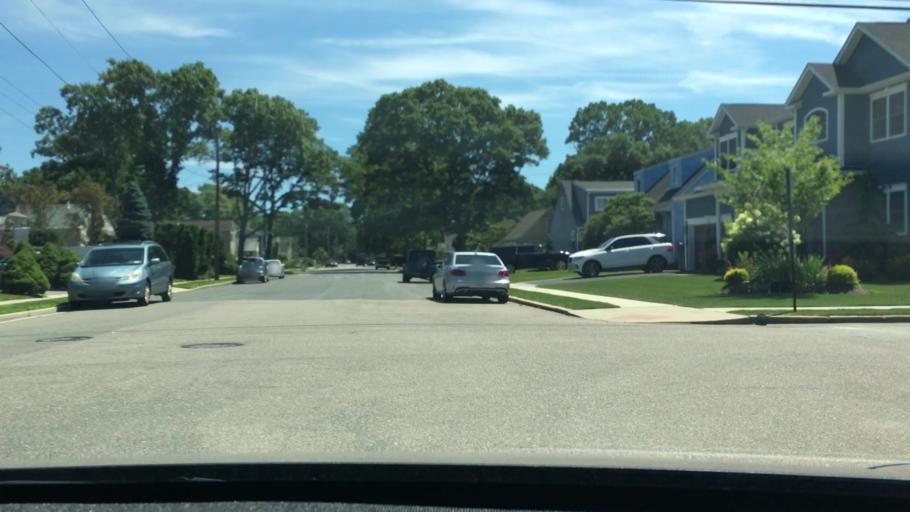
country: US
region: New York
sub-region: Nassau County
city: Massapequa Park
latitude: 40.6763
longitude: -73.4601
